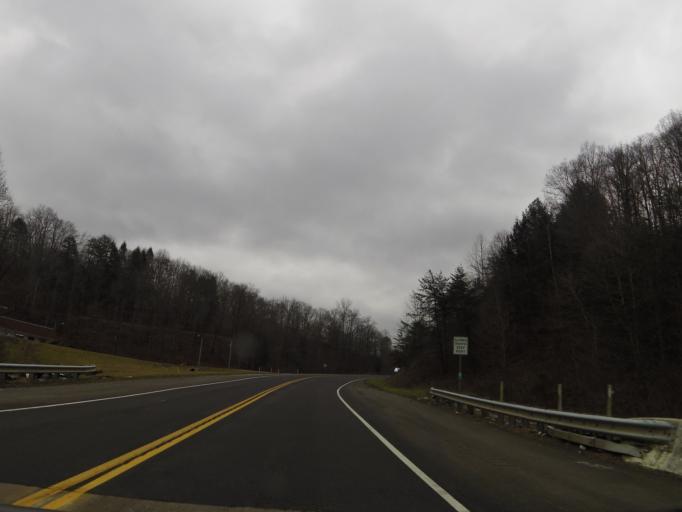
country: US
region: Tennessee
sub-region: Scott County
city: Huntsville
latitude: 36.3821
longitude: -84.4131
